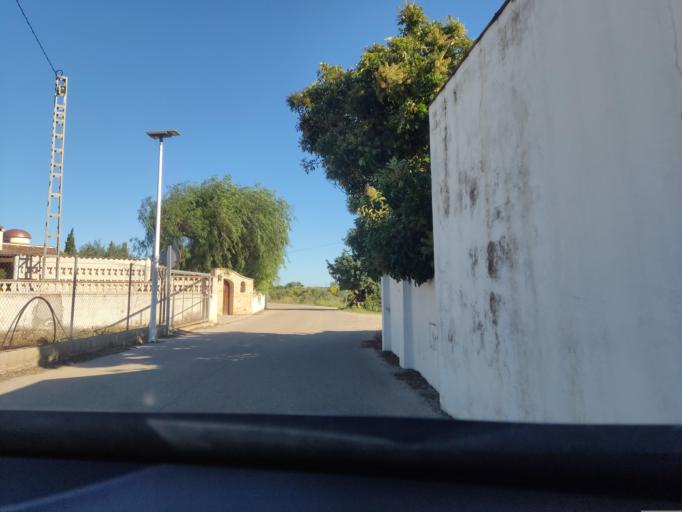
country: ES
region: Valencia
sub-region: Provincia de Alicante
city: els Poblets
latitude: 38.8527
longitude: 0.0251
